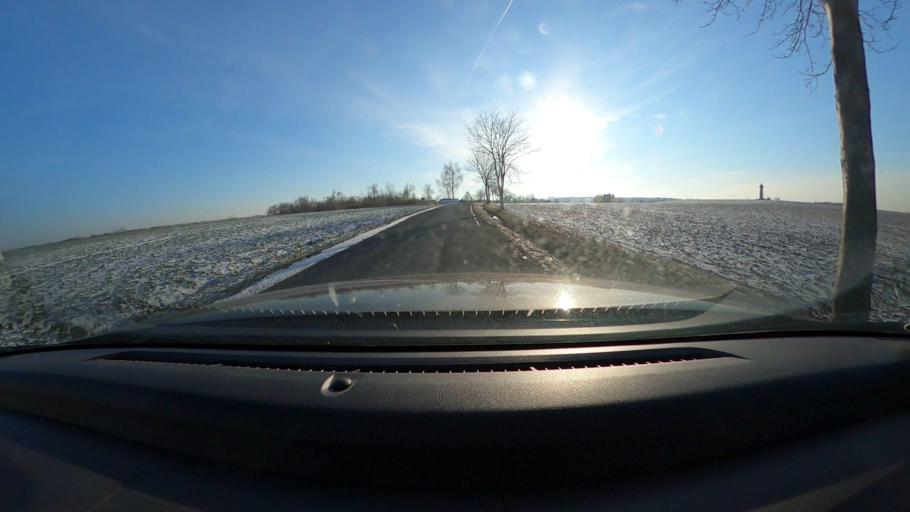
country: DE
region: Saxony
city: Frankenstein
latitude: 50.9470
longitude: 13.2249
